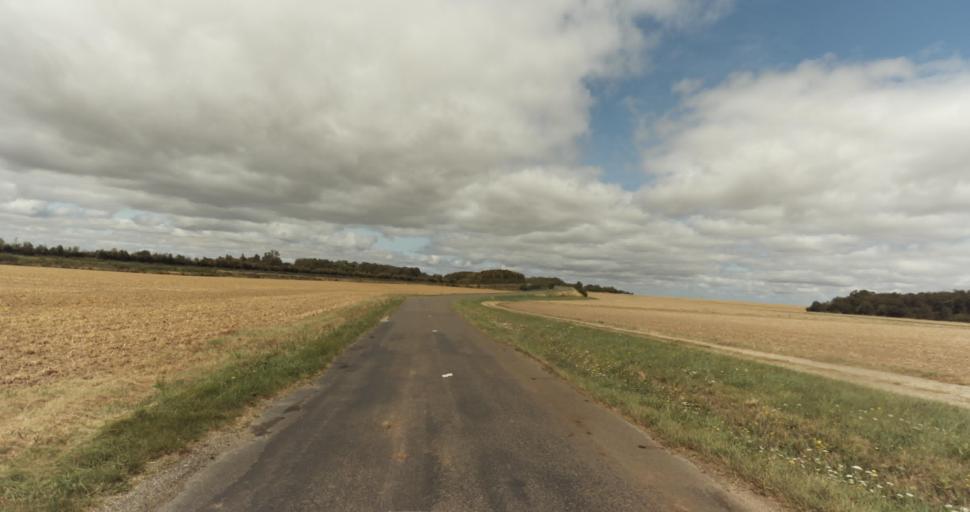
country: FR
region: Haute-Normandie
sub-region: Departement de l'Eure
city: Evreux
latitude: 48.9219
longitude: 1.2058
